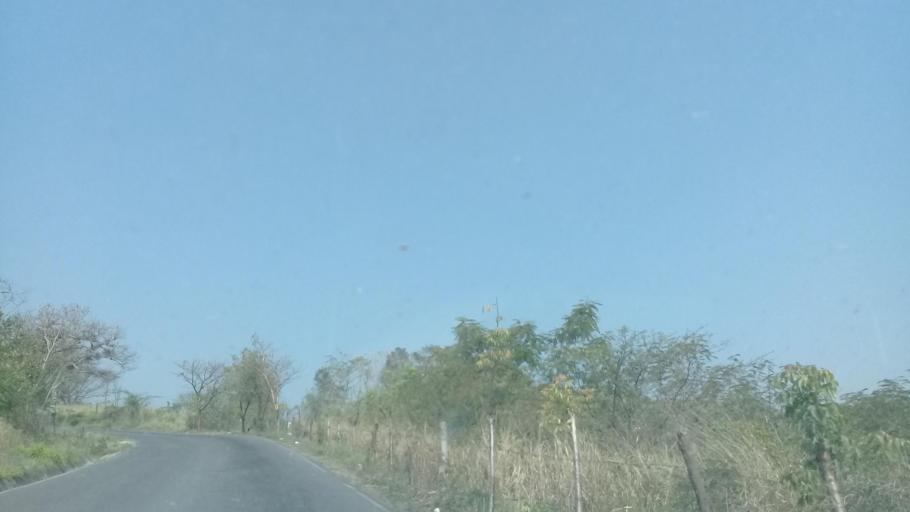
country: MX
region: Veracruz
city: El Castillo
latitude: 19.5772
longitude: -96.8304
